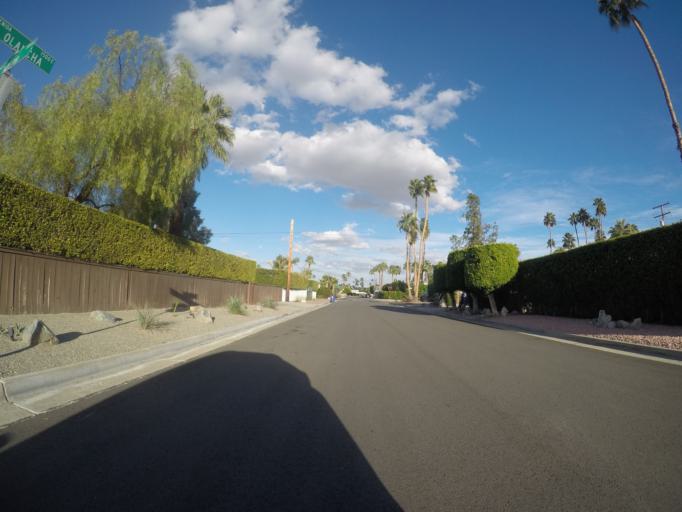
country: US
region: California
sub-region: Riverside County
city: Palm Springs
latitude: 33.8032
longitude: -116.5299
